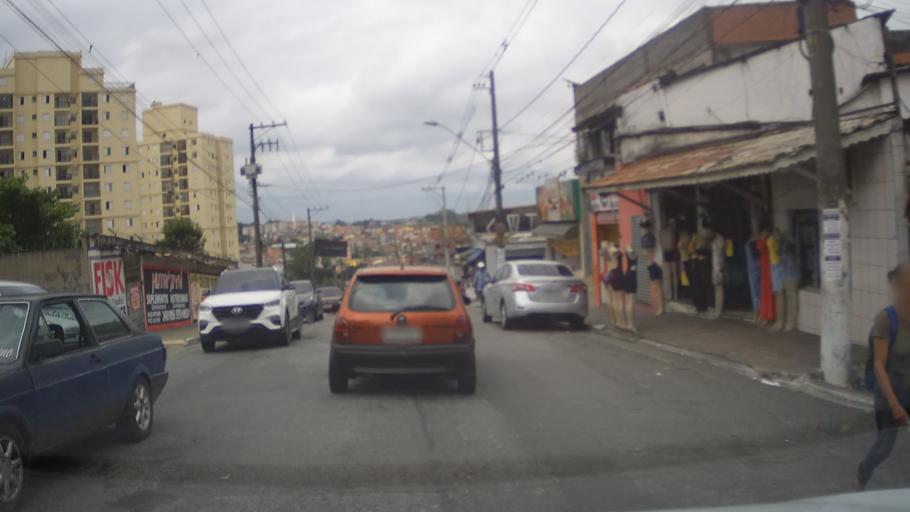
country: BR
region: Sao Paulo
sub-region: Itaquaquecetuba
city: Itaquaquecetuba
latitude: -23.4531
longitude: -46.4057
